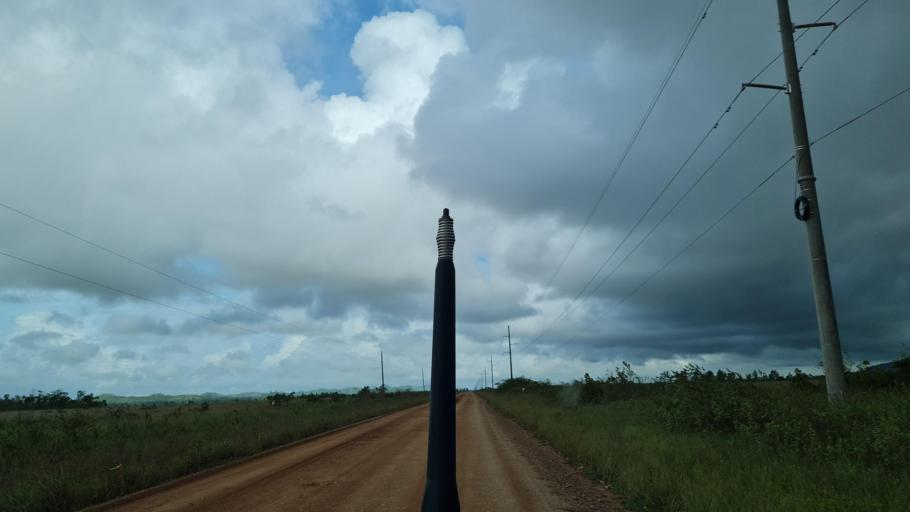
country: NI
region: Atlantico Norte (RAAN)
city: Puerto Cabezas
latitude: 14.1102
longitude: -83.6055
